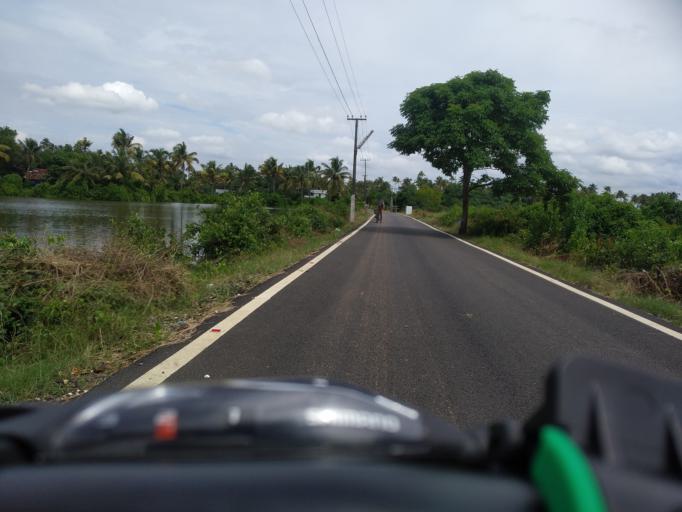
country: IN
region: Kerala
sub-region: Ernakulam
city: Elur
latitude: 10.0806
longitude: 76.2171
